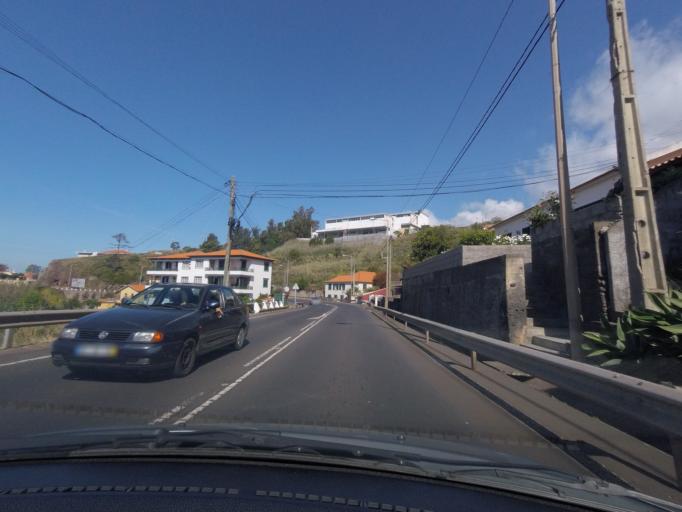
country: PT
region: Madeira
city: Canico
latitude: 32.6484
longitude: -16.8548
